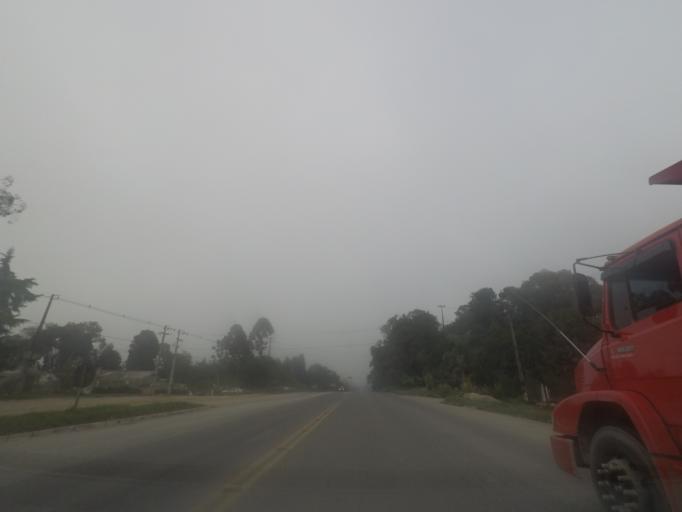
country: BR
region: Parana
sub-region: Almirante Tamandare
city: Almirante Tamandare
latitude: -25.2683
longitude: -49.3032
